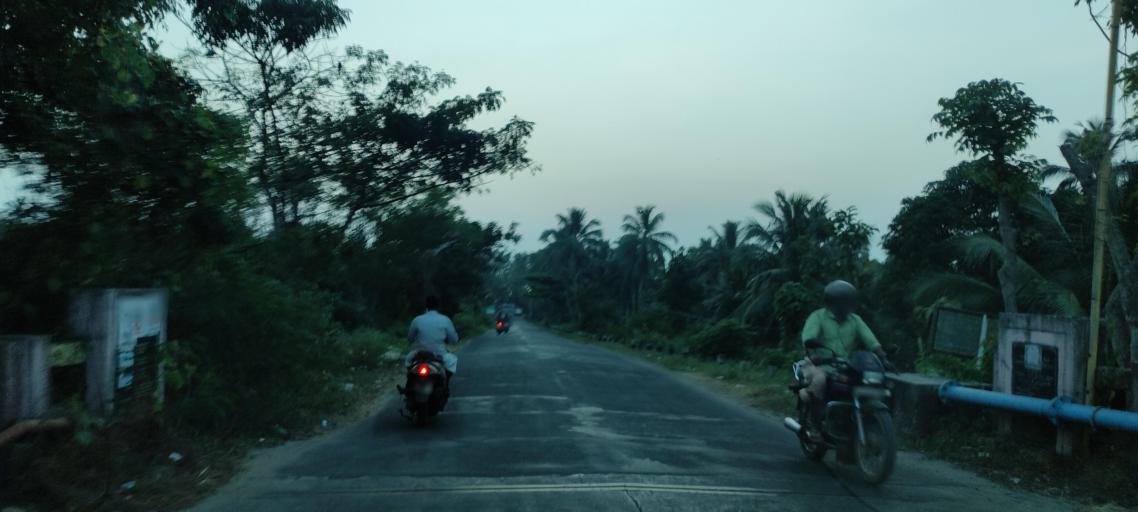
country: IN
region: Kerala
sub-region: Alappuzha
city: Kayankulam
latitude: 9.1149
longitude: 76.4757
